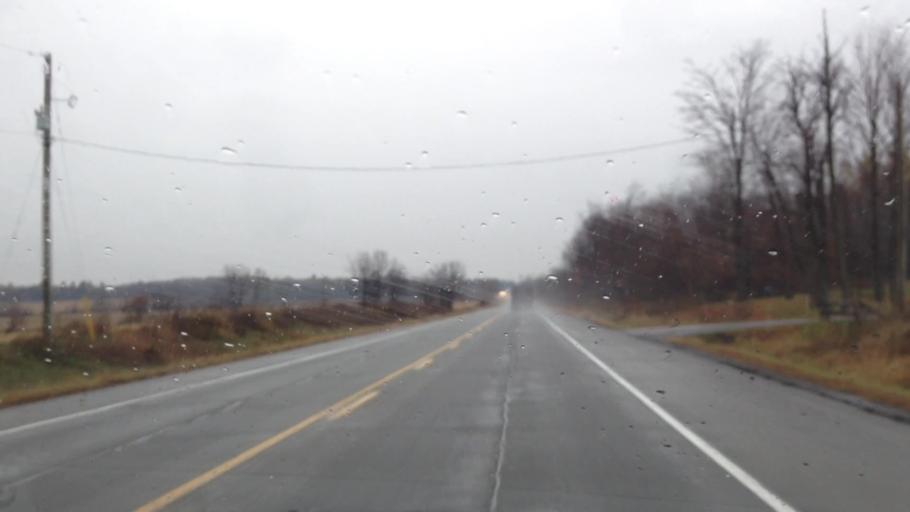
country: CA
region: Ontario
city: Clarence-Rockland
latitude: 45.3921
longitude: -75.3915
